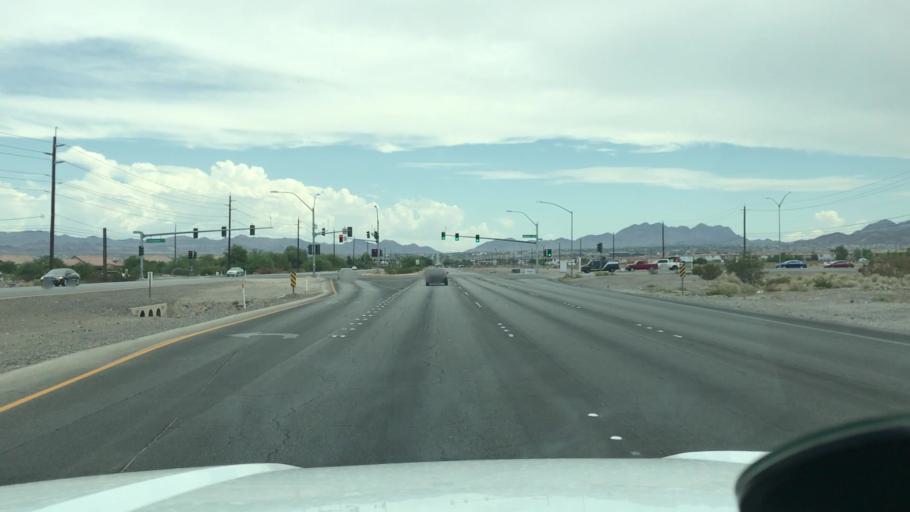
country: US
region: Nevada
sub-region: Clark County
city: Henderson
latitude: 36.0764
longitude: -115.0237
